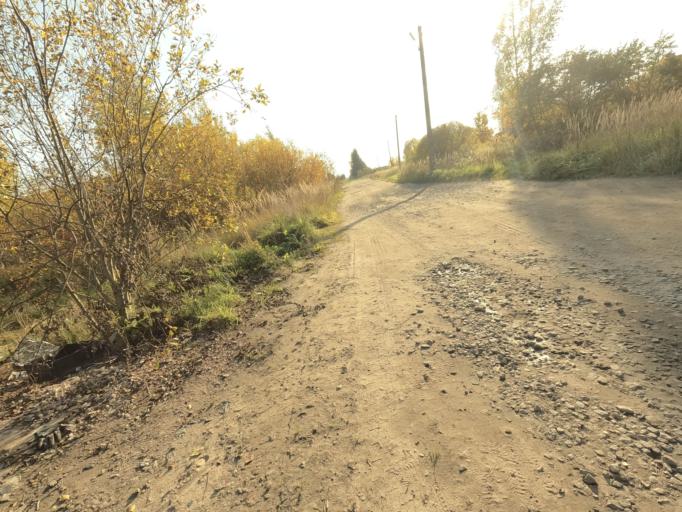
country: RU
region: Leningrad
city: Mga
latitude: 59.7525
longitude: 31.0677
